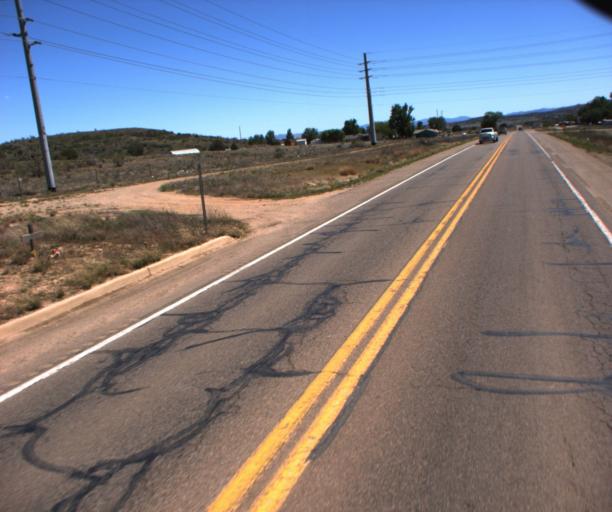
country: US
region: Arizona
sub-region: Yavapai County
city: Paulden
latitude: 34.8889
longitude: -112.4676
